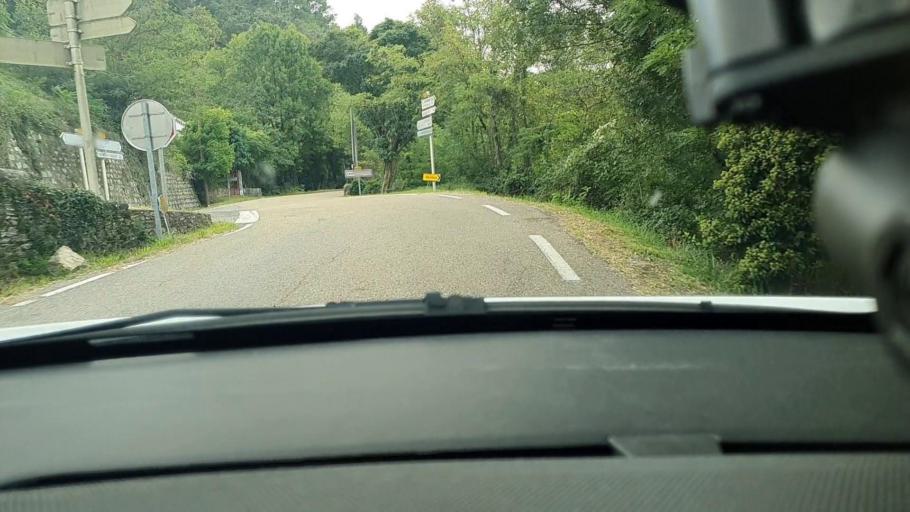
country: FR
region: Languedoc-Roussillon
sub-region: Departement du Gard
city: Branoux-les-Taillades
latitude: 44.3032
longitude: 3.9792
